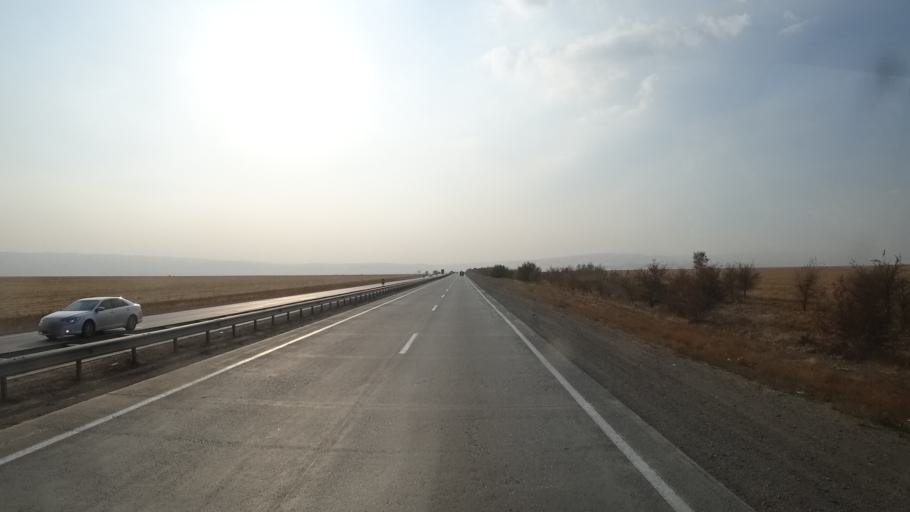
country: KZ
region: Zhambyl
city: Taraz
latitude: 42.8069
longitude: 71.1160
